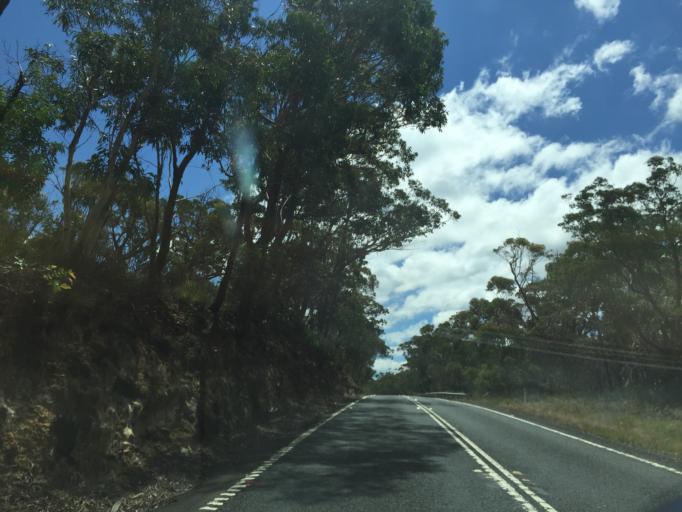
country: AU
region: New South Wales
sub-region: Blue Mountains Municipality
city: Blackheath
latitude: -33.5701
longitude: 150.3511
